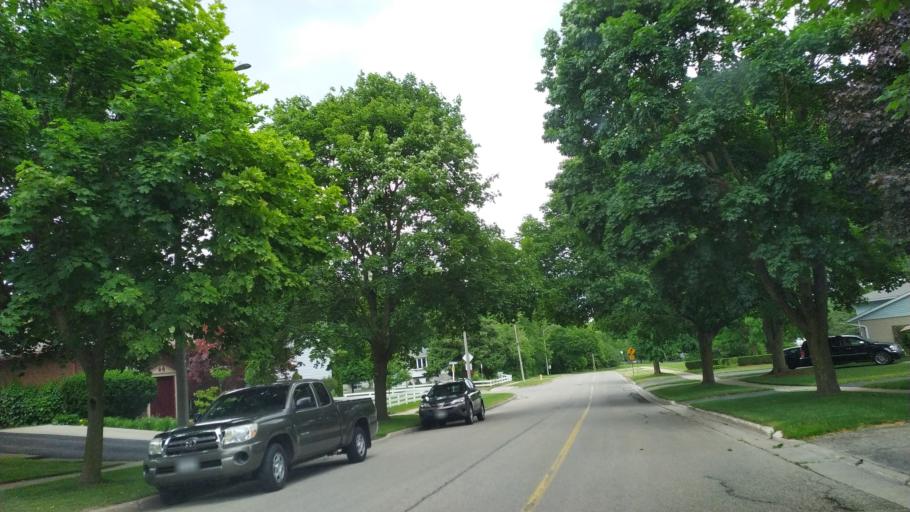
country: CA
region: Ontario
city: Kitchener
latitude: 43.4432
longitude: -80.5331
